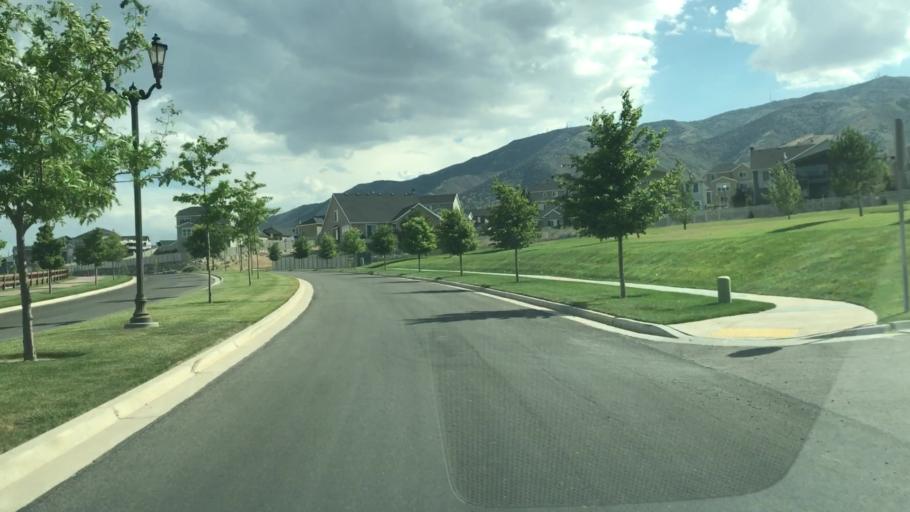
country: US
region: Utah
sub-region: Utah County
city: Saratoga Springs
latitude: 40.3082
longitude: -111.9002
